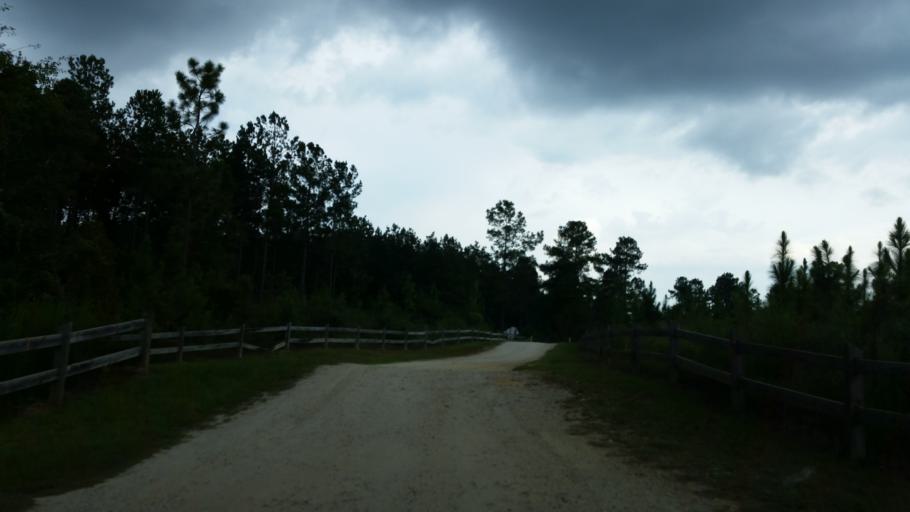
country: US
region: Florida
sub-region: Escambia County
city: Cantonment
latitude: 30.6776
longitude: -87.4016
